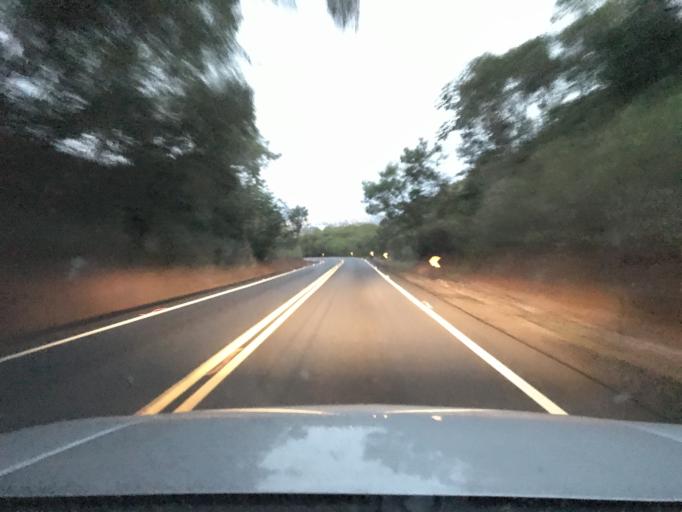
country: PY
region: Canindeyu
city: Salto del Guaira
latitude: -24.0317
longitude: -54.2868
